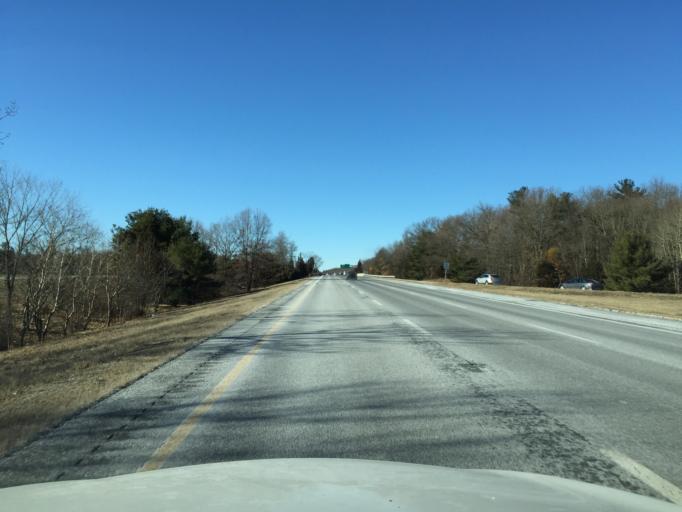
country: US
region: Massachusetts
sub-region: Norfolk County
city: Wrentham
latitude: 42.0373
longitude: -71.3034
